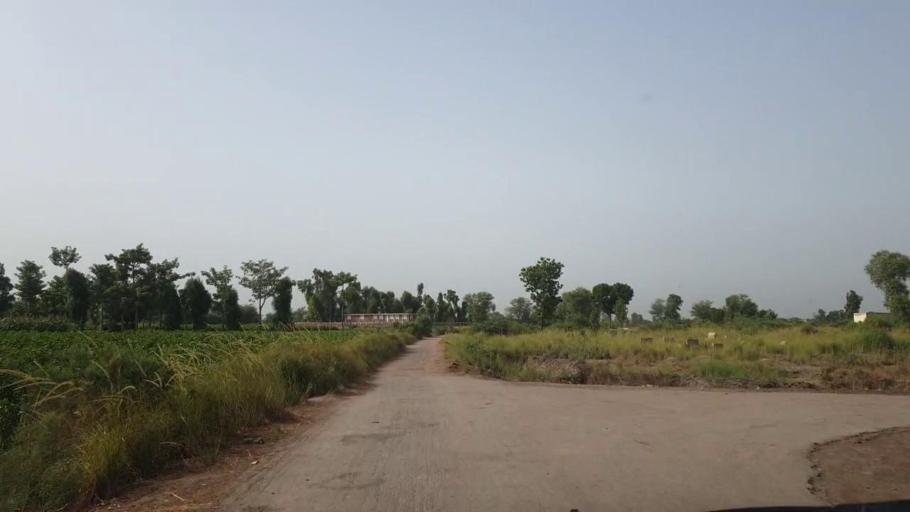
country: PK
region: Sindh
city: Nawabshah
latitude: 26.2262
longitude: 68.4226
